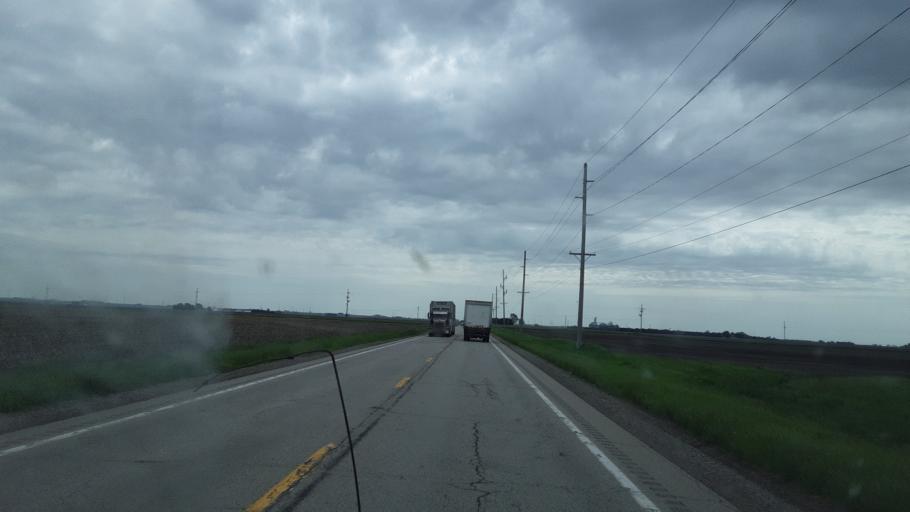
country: US
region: Illinois
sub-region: Tazewell County
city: Delavan
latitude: 40.3067
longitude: -89.5315
